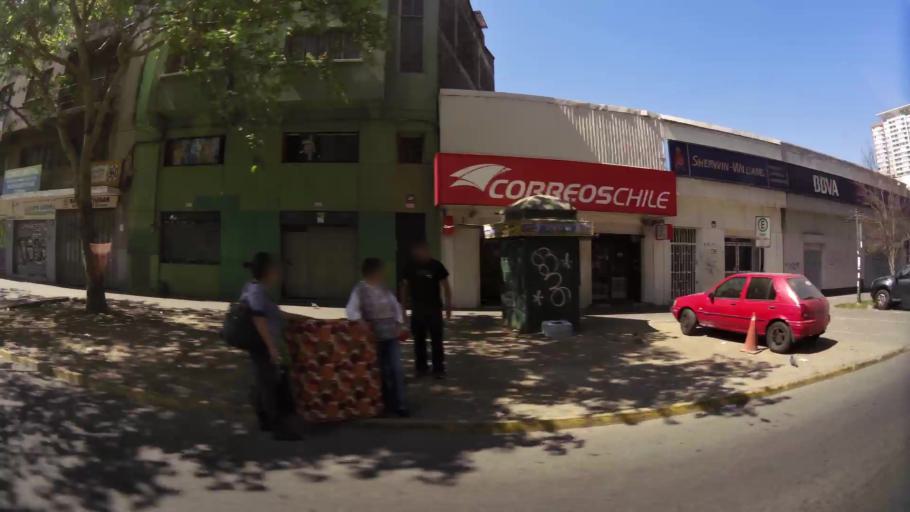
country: CL
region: Santiago Metropolitan
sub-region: Provincia de Santiago
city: Santiago
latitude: -33.4529
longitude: -70.6305
